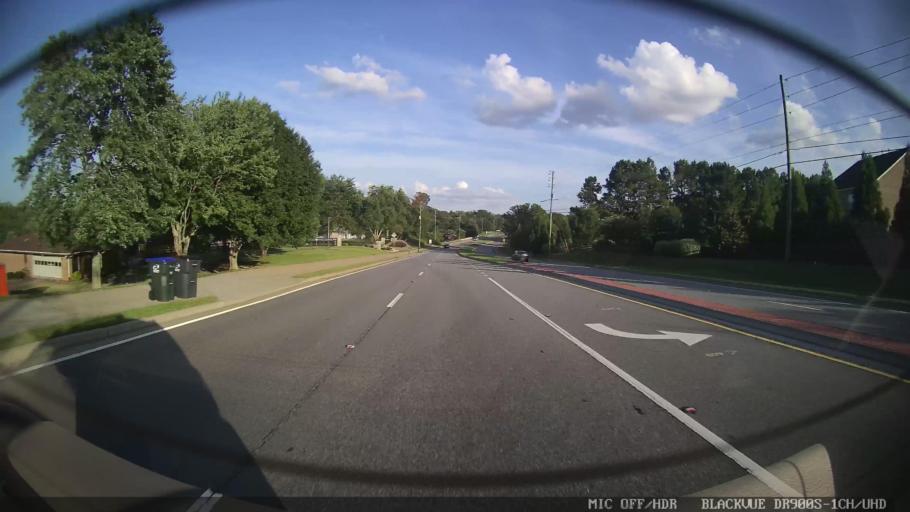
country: US
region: Georgia
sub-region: Fulton County
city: Milton
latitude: 34.1452
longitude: -84.2360
